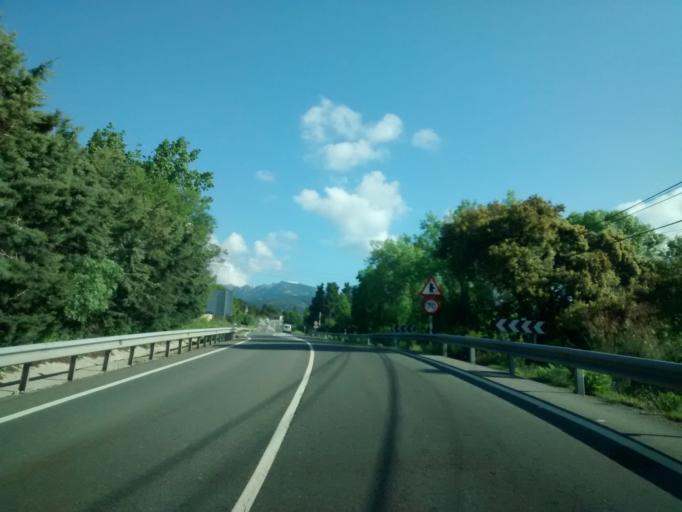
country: ES
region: Madrid
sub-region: Provincia de Madrid
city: Becerril de la Sierra
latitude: 40.7045
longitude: -4.0040
